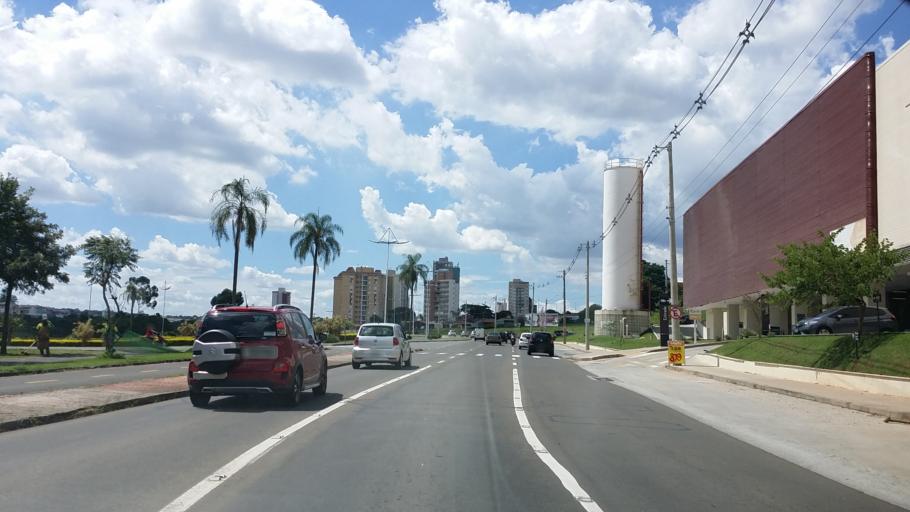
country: BR
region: Sao Paulo
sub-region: Indaiatuba
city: Indaiatuba
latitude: -23.0949
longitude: -47.2255
